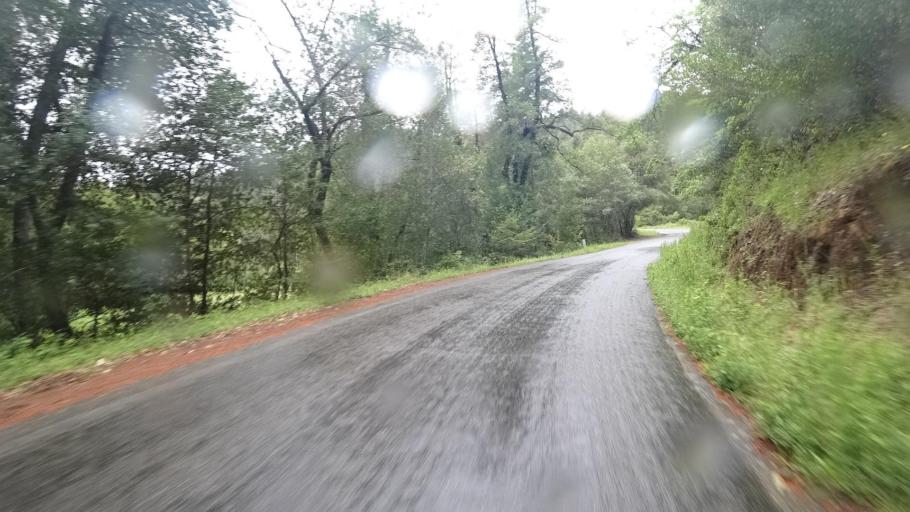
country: US
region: California
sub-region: Siskiyou County
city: Happy Camp
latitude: 41.3719
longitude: -123.5006
